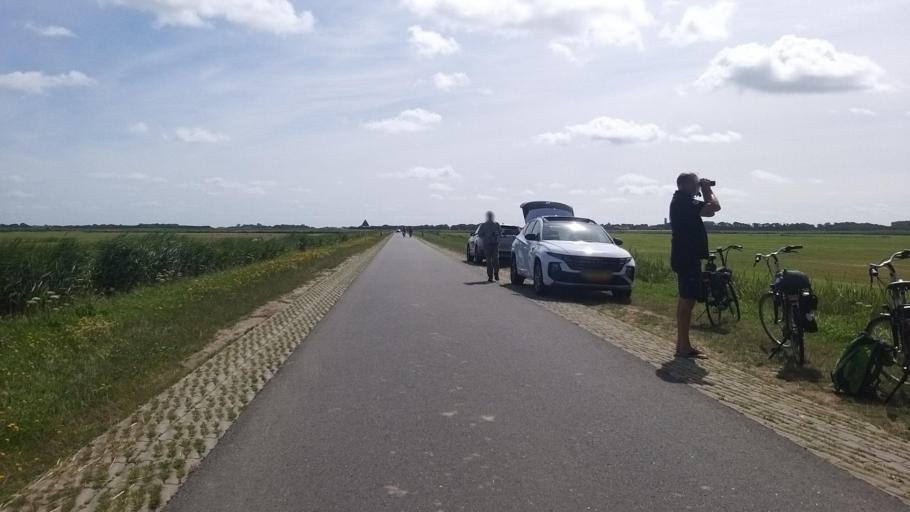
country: NL
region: North Holland
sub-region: Gemeente Texel
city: Den Burg
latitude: 53.0829
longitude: 4.8013
